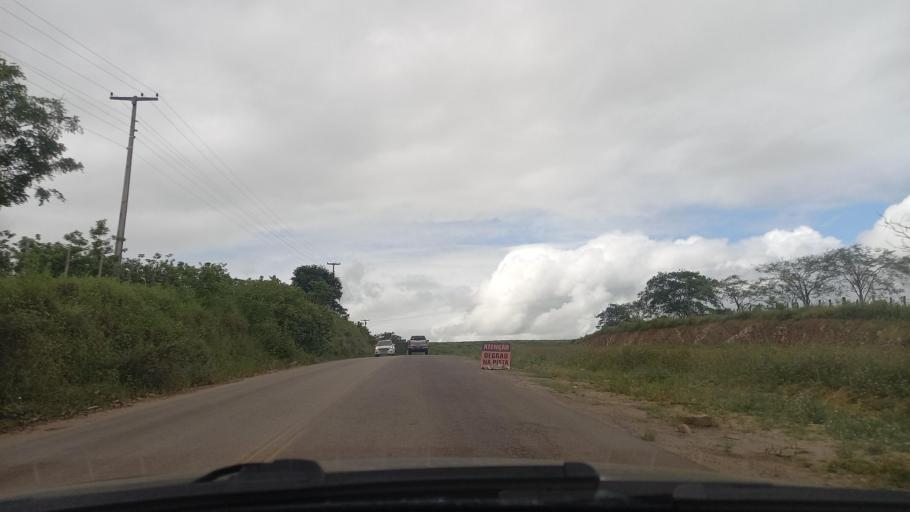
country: BR
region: Alagoas
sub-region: Batalha
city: Batalha
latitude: -9.6355
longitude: -37.1974
